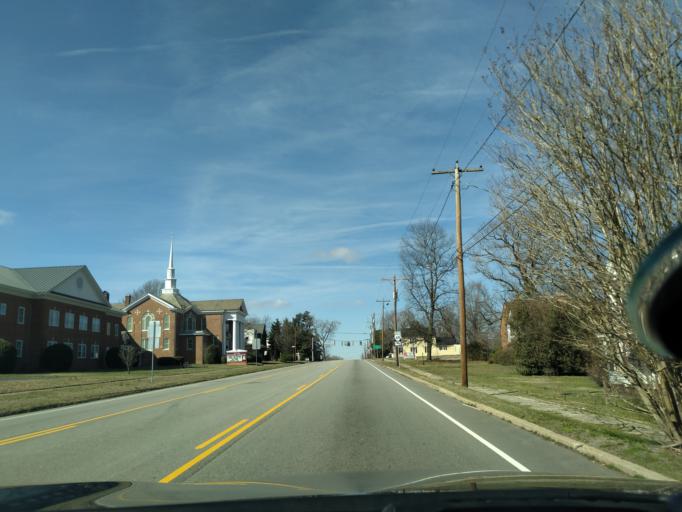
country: US
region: Virginia
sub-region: Nottoway County
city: Crewe
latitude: 37.1712
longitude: -78.1211
